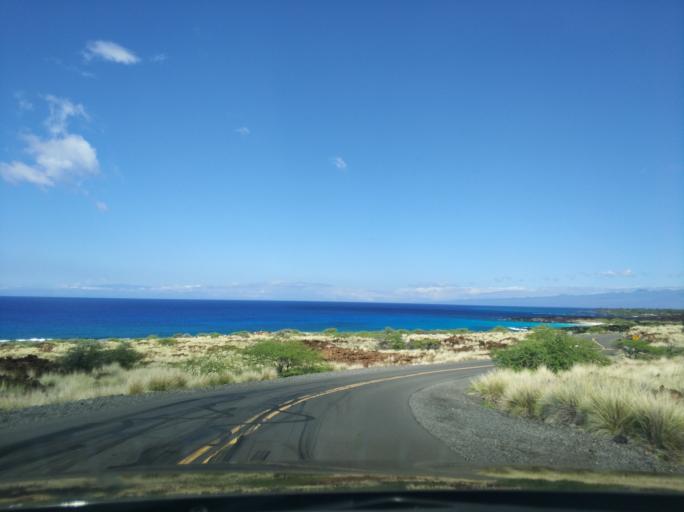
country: US
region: Hawaii
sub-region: Hawaii County
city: Kalaoa
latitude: 19.8039
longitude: -156.0112
